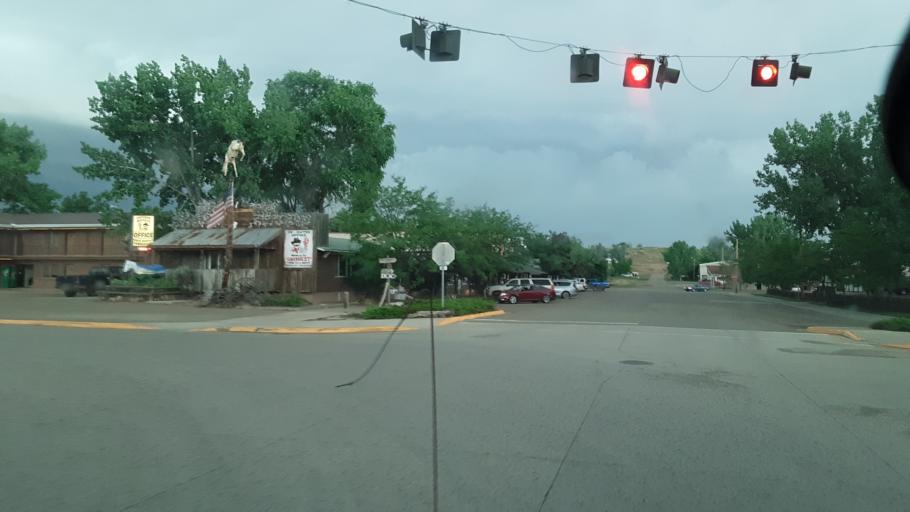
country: US
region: Montana
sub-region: Powder River County
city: Broadus
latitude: 45.4433
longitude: -105.4084
